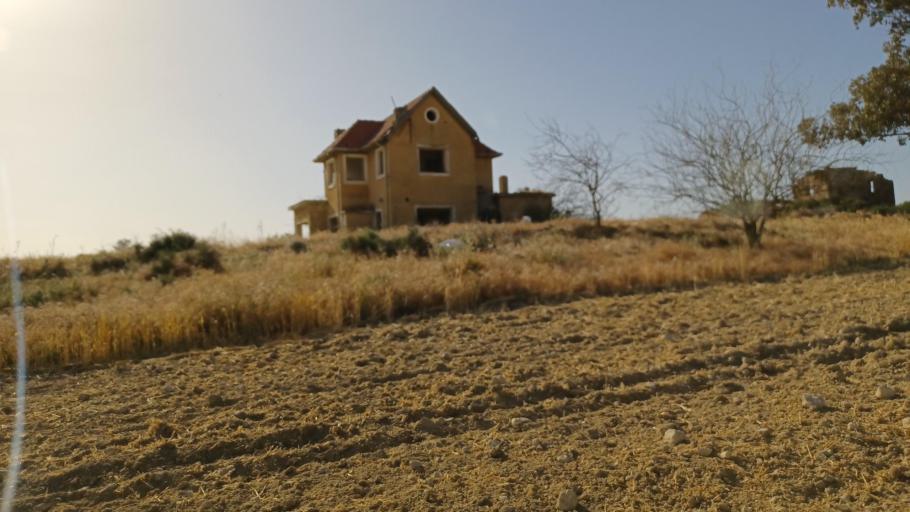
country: CY
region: Lefkosia
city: Mammari
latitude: 35.1683
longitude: 33.2460
